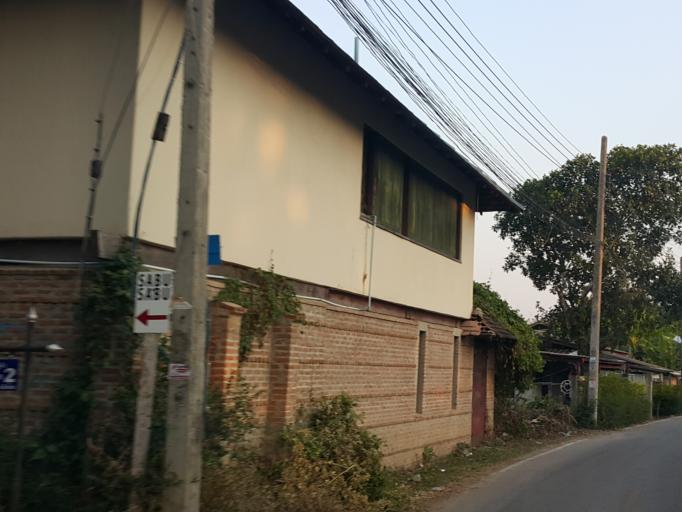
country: TH
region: Chiang Mai
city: San Sai
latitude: 18.8863
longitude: 98.9669
